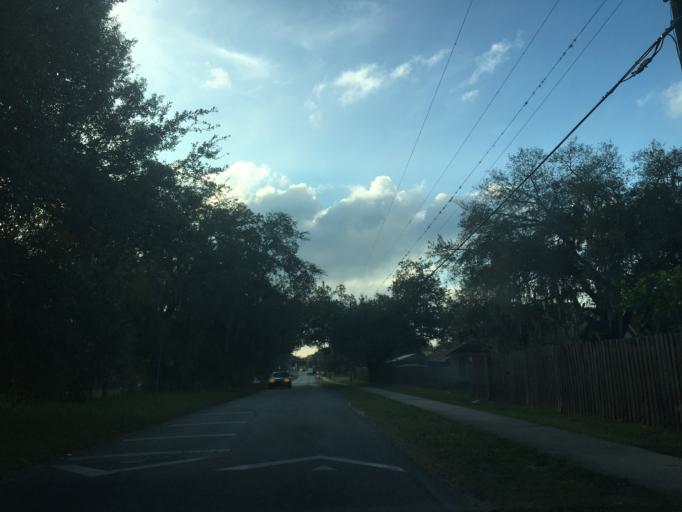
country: US
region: Florida
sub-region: Hillsborough County
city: Temple Terrace
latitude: 28.0253
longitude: -82.4075
